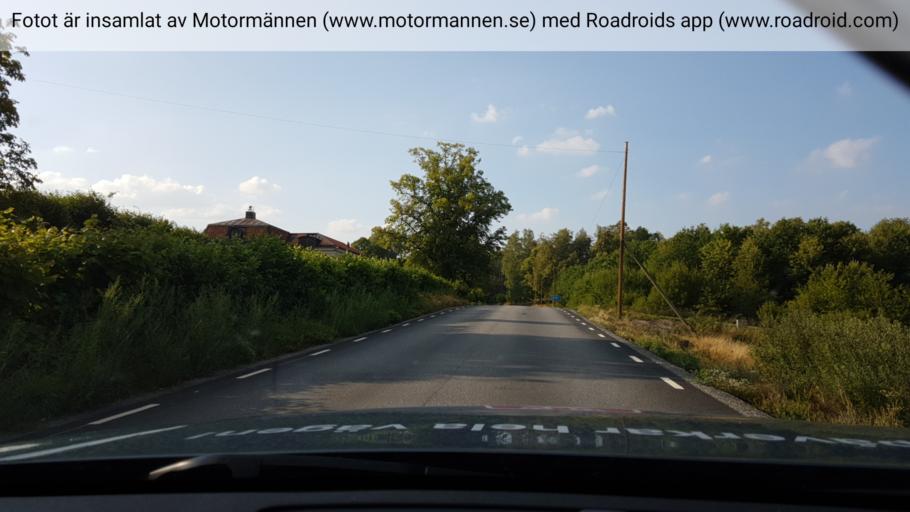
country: SE
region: Soedermanland
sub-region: Strangnas Kommun
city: Mariefred
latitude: 59.1384
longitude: 17.2141
